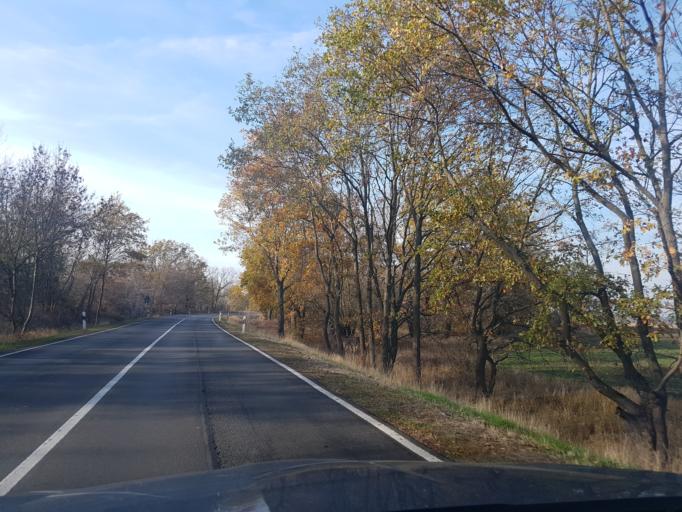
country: DE
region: Saxony
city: Beilrode
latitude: 51.5530
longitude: 13.0400
